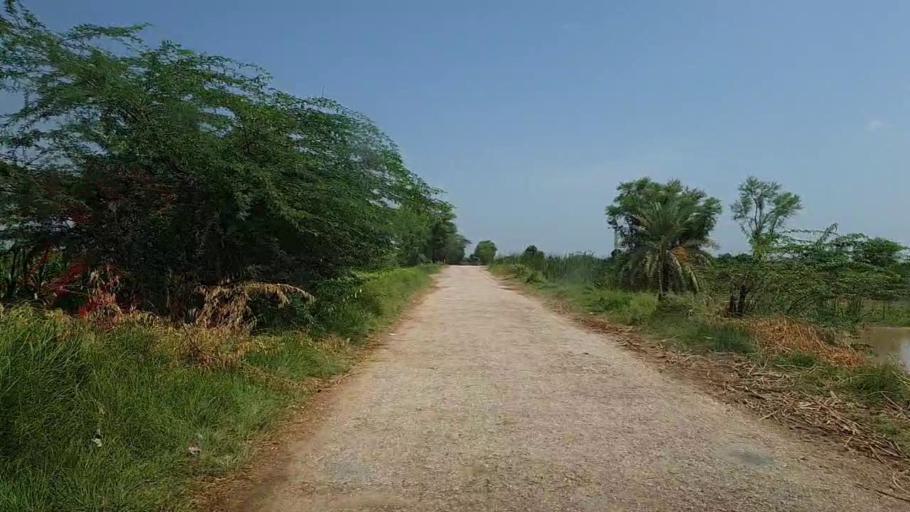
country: PK
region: Sindh
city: Bhiria
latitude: 26.8957
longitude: 68.1967
